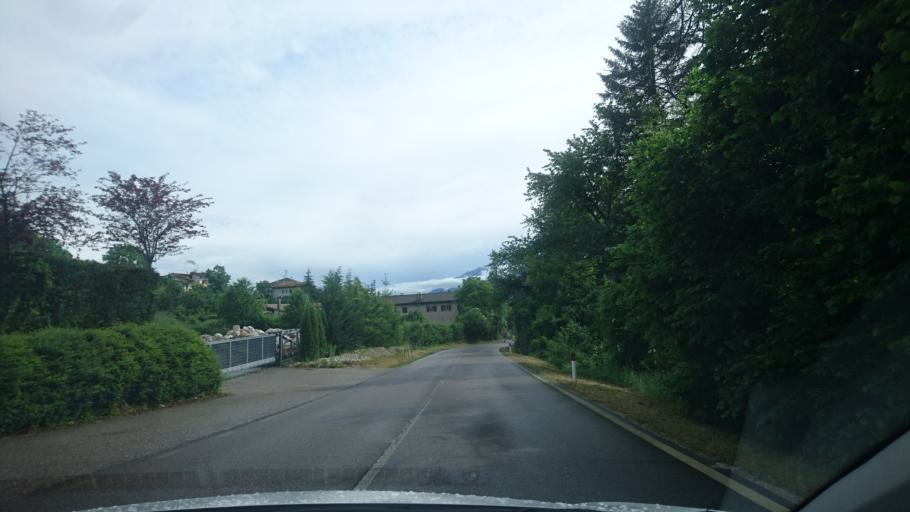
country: IT
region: Trentino-Alto Adige
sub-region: Provincia di Trento
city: Dambel
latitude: 46.3827
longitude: 11.0922
